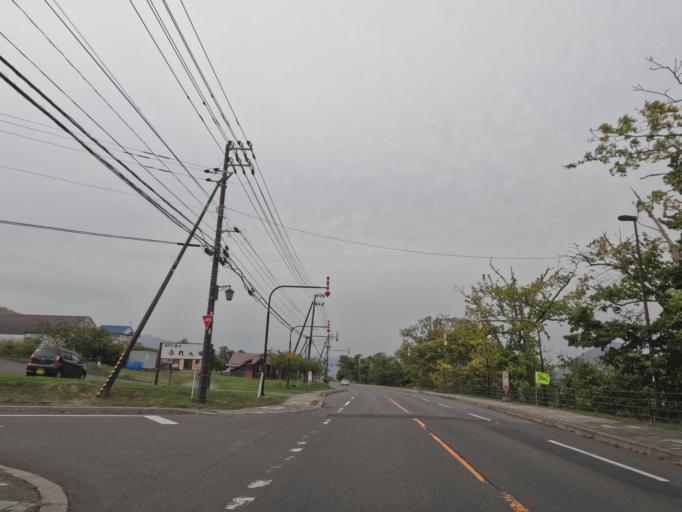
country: JP
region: Hokkaido
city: Date
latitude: 42.5588
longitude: 140.8542
